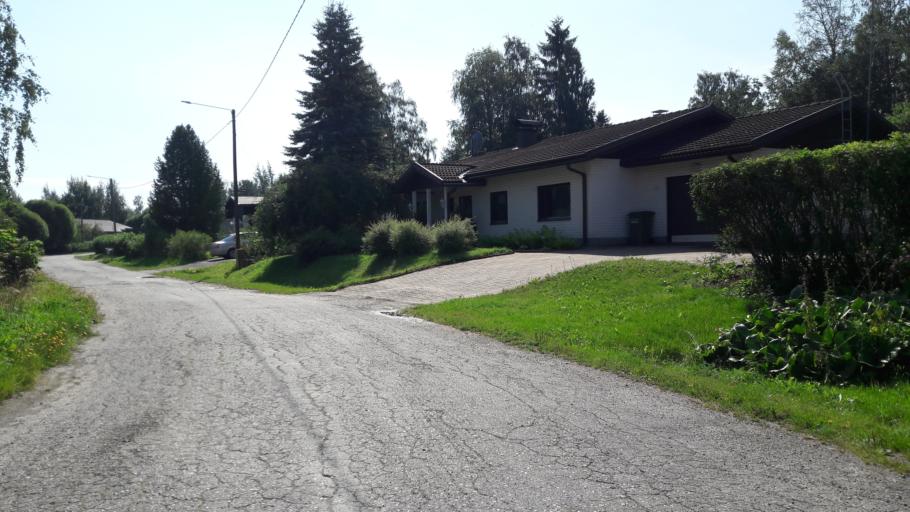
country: FI
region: North Karelia
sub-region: Joensuu
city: Joensuu
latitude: 62.5328
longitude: 29.8359
